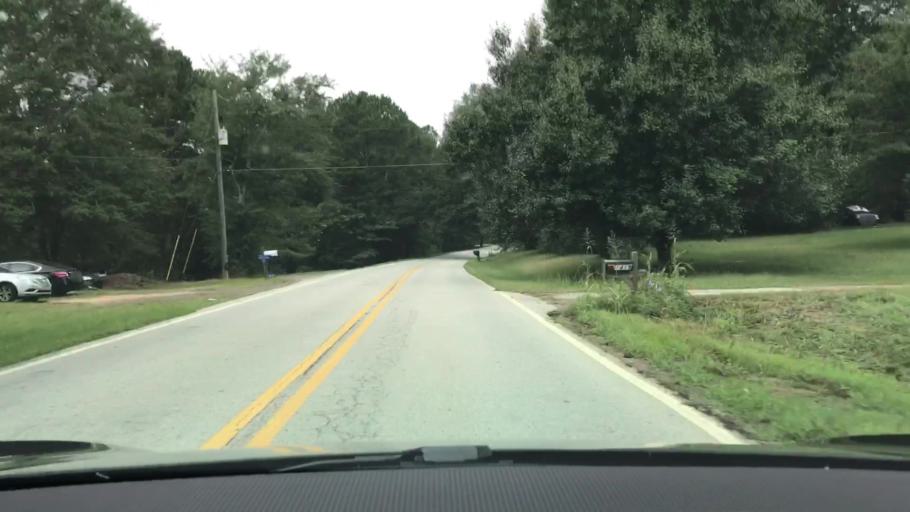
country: US
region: Georgia
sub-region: Barrow County
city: Auburn
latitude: 34.0567
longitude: -83.8283
